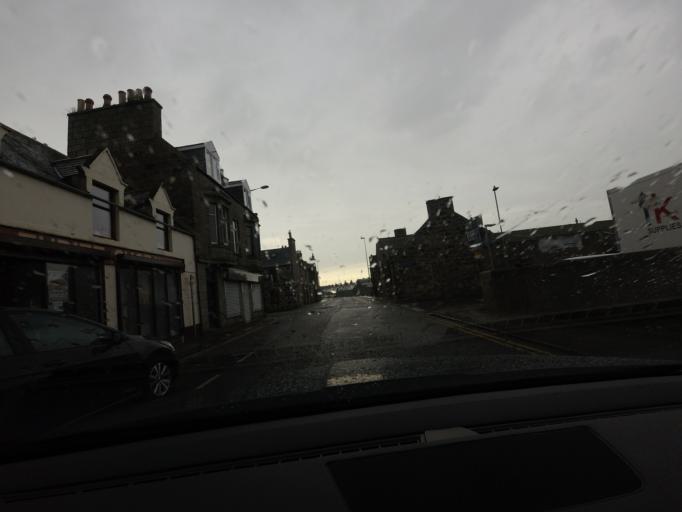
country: GB
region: Scotland
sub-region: Aberdeenshire
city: Fraserburgh
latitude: 57.6941
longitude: -2.0090
